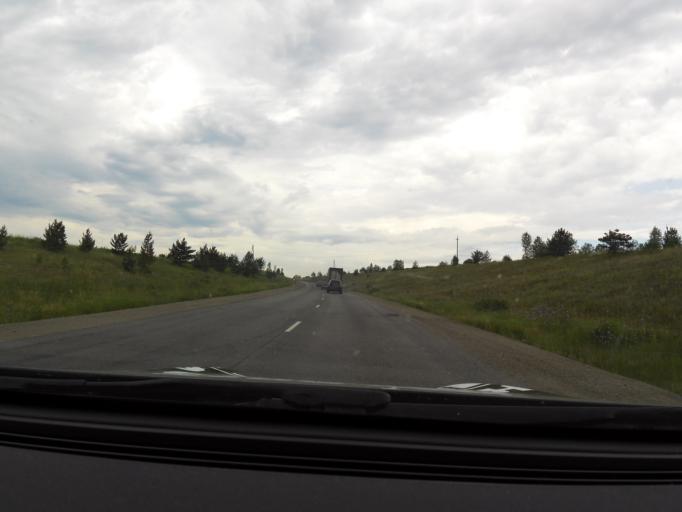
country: RU
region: Chelyabinsk
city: Sim
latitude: 55.0073
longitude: 57.6808
